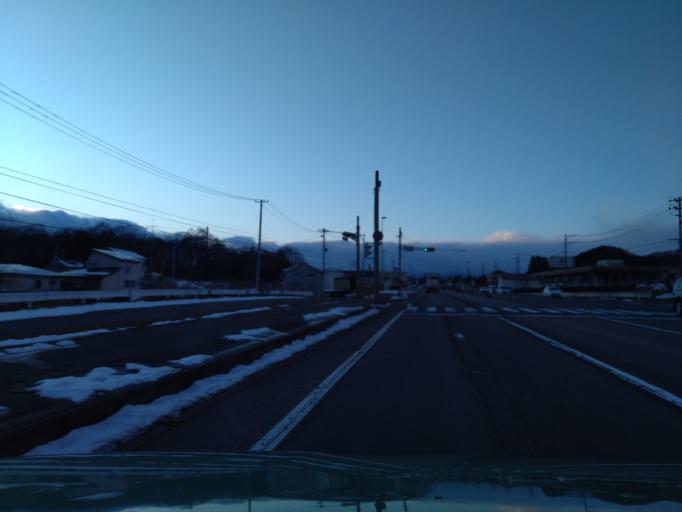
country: JP
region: Iwate
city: Shizukuishi
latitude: 39.6999
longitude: 141.0538
